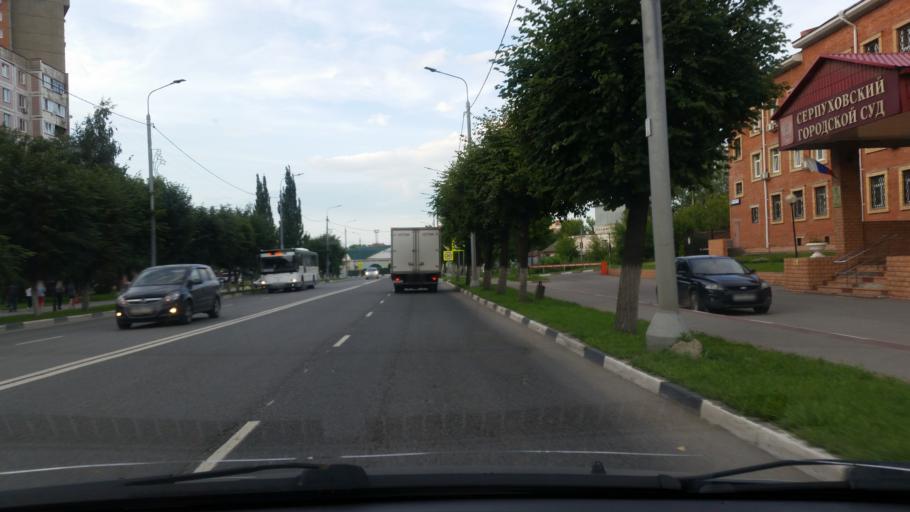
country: RU
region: Moskovskaya
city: Serpukhov
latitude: 54.9275
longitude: 37.4493
